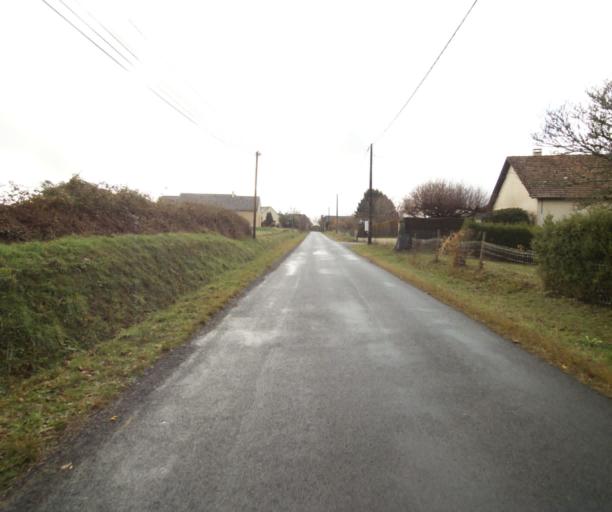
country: FR
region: Limousin
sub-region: Departement de la Correze
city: Cornil
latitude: 45.2216
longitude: 1.6441
